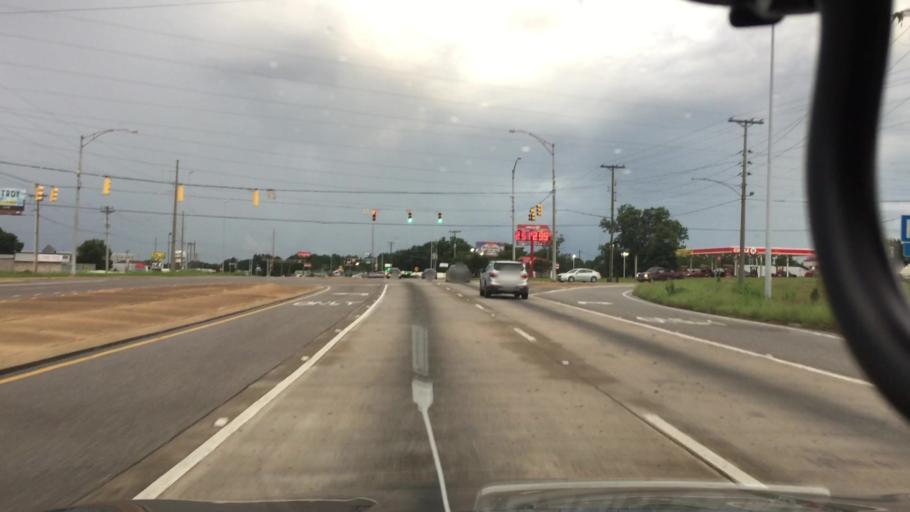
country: US
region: Alabama
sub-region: Pike County
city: Troy
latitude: 31.7929
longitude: -85.9782
